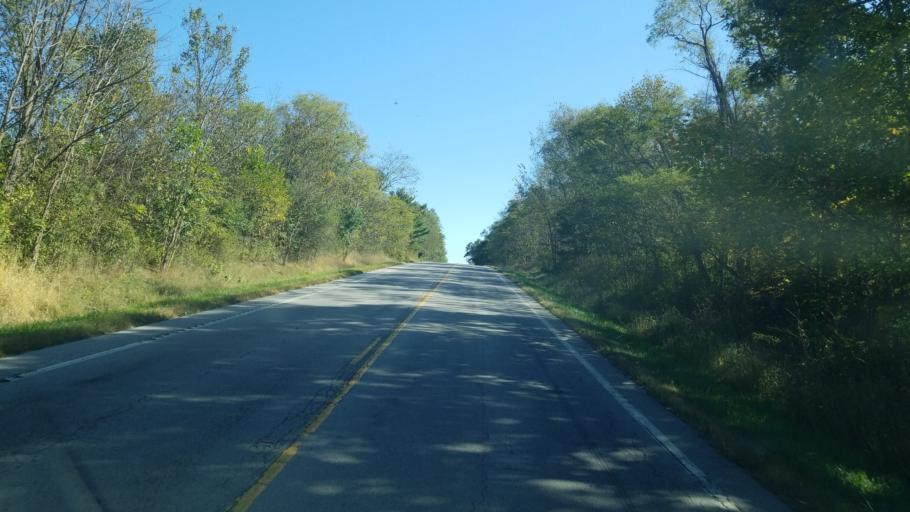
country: US
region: Ohio
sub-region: Huron County
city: New London
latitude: 40.9989
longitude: -82.3950
